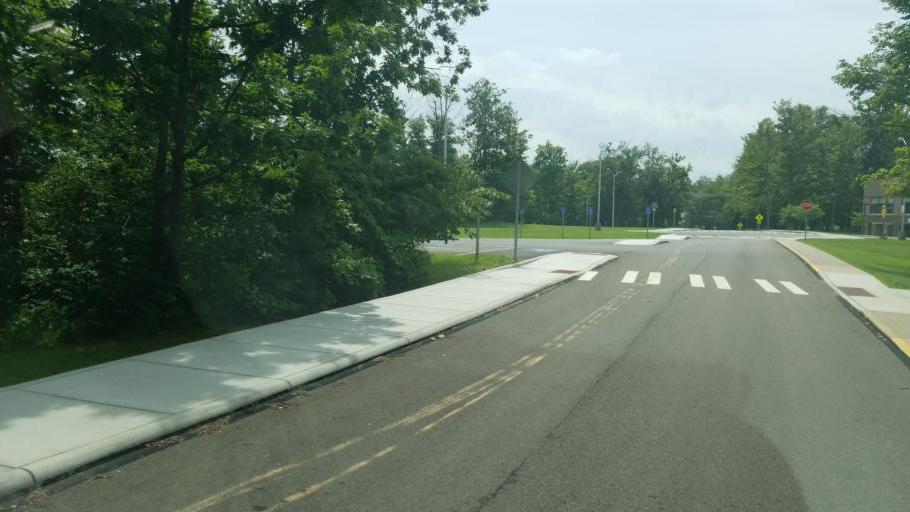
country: US
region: Ohio
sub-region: Richland County
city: Ontario
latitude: 40.8001
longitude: -82.5808
